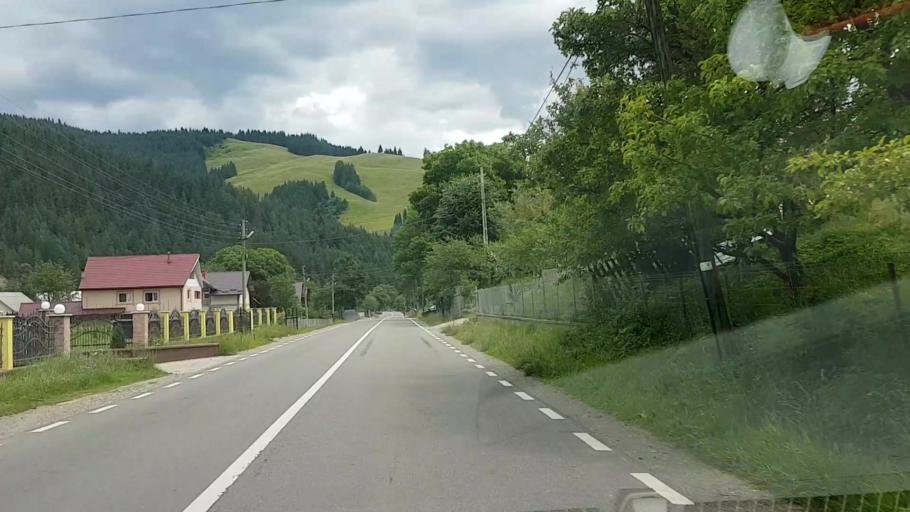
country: RO
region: Neamt
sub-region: Comuna Farcasa
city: Farcasa
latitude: 47.1356
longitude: 25.8886
